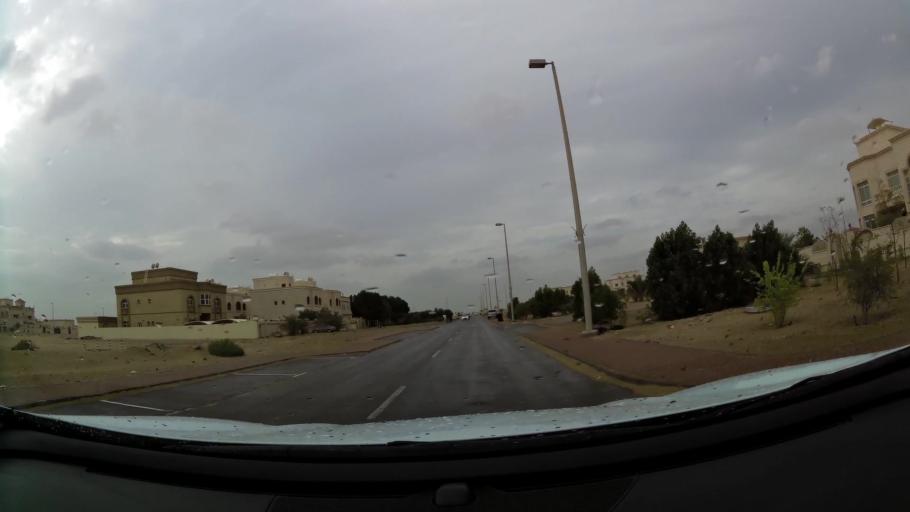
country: AE
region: Abu Dhabi
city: Abu Dhabi
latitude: 24.3614
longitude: 54.6211
